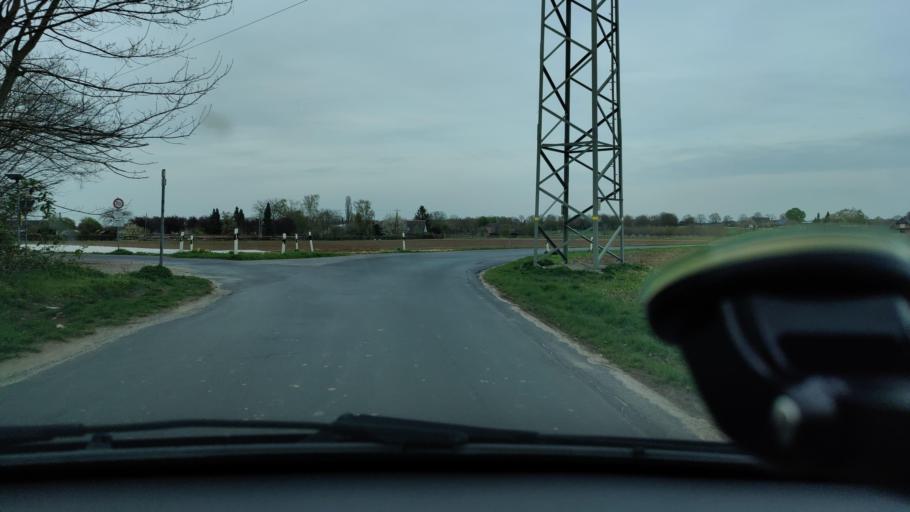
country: DE
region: North Rhine-Westphalia
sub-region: Regierungsbezirk Dusseldorf
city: Goch
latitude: 51.7372
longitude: 6.1921
